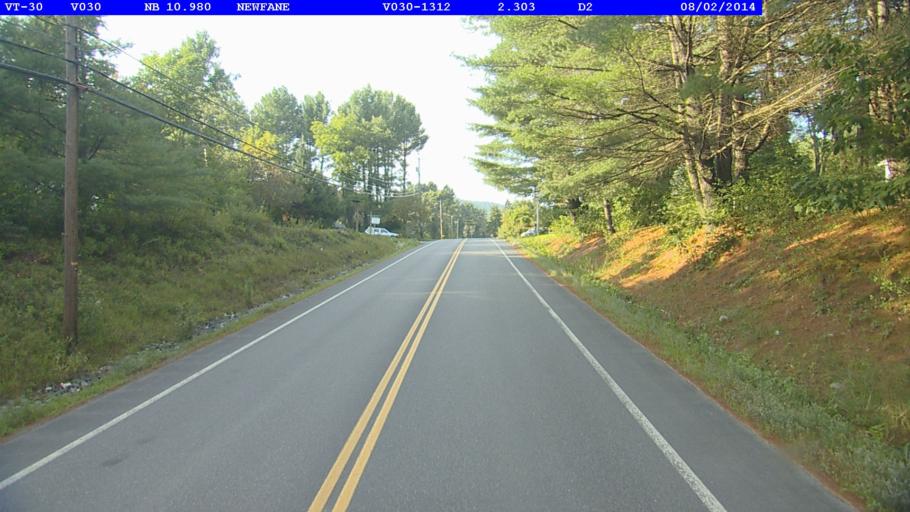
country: US
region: Vermont
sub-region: Windham County
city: Newfane
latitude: 42.9771
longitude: -72.6574
